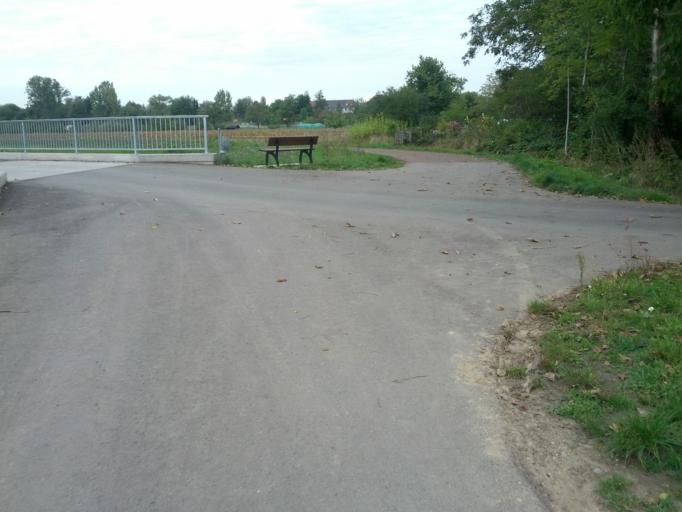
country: DE
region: Baden-Wuerttemberg
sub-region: Freiburg Region
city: Kenzingen
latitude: 48.1868
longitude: 7.7751
